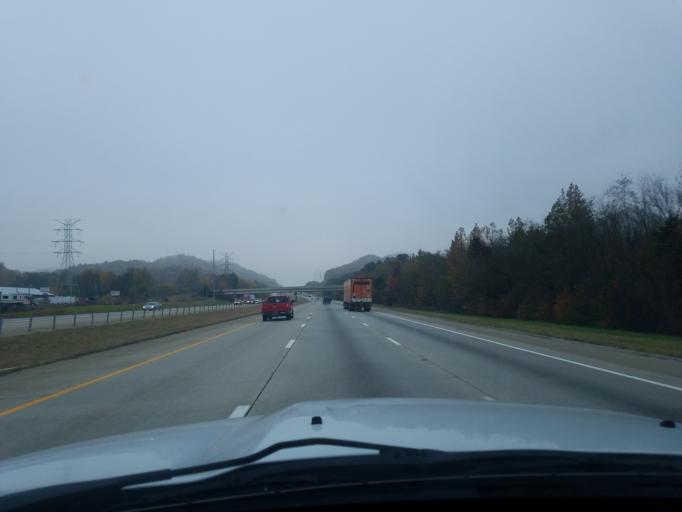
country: US
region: Kentucky
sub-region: Bullitt County
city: Lebanon Junction
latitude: 37.8695
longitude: -85.7042
